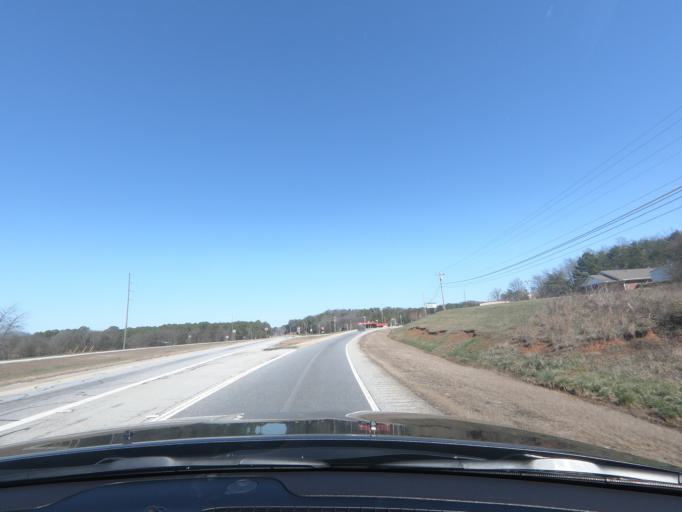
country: US
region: Georgia
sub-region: Gordon County
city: Calhoun
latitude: 34.4690
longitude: -84.9758
